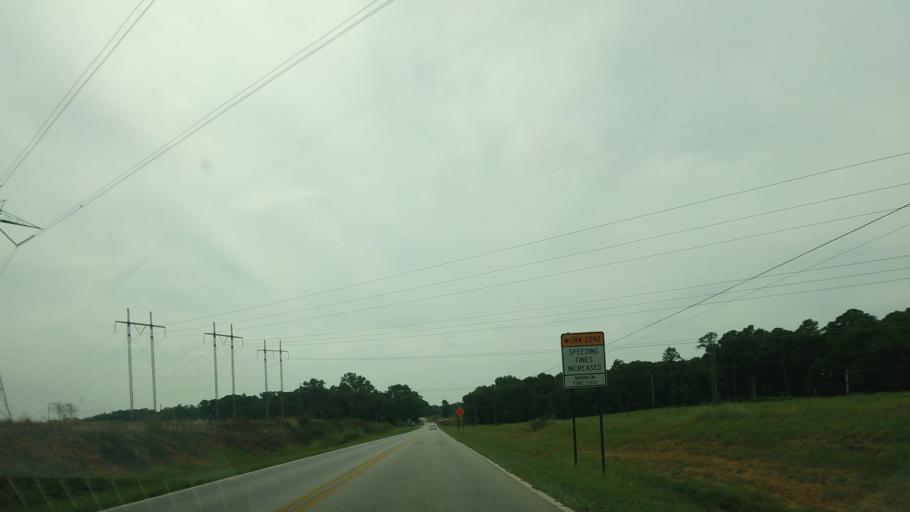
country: US
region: Georgia
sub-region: Houston County
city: Robins Air Force Base
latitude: 32.5585
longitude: -83.5863
